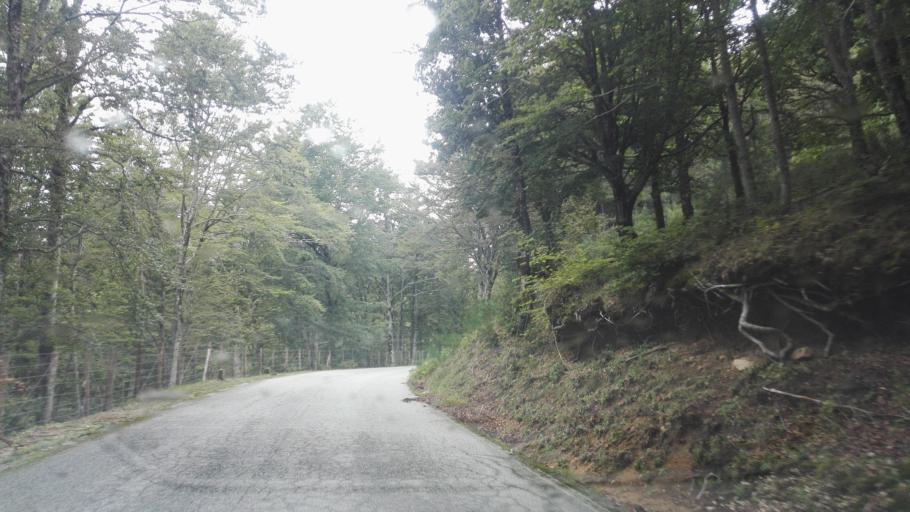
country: IT
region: Calabria
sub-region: Provincia di Vibo-Valentia
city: Nardodipace
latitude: 38.4883
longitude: 16.3751
